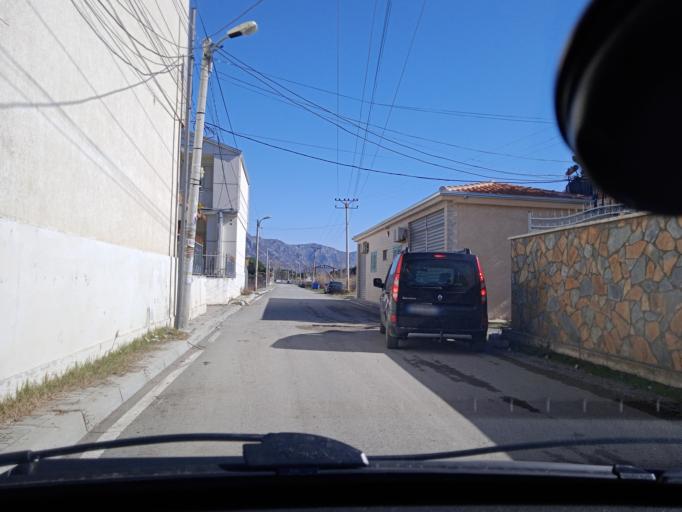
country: AL
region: Shkoder
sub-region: Rrethi i Shkodres
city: Velipoje
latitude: 41.8627
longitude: 19.4364
